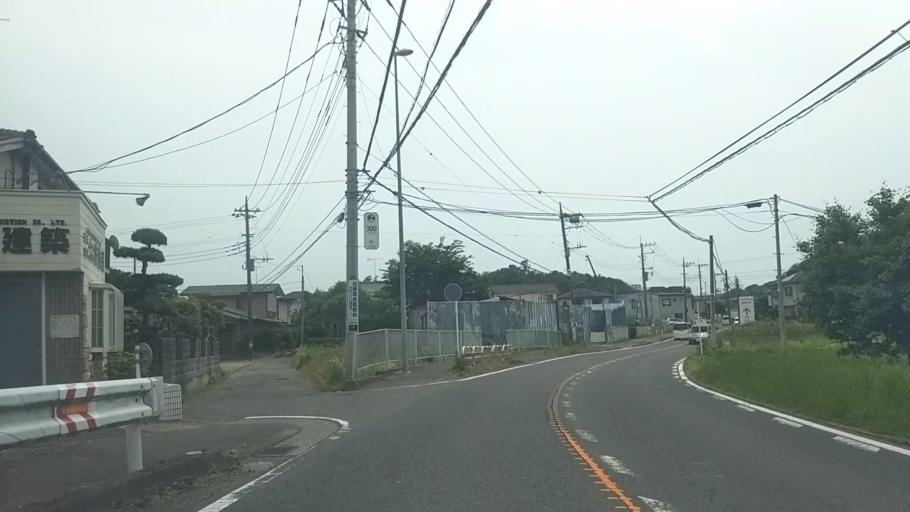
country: JP
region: Kanagawa
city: Chigasaki
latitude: 35.3627
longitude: 139.4220
